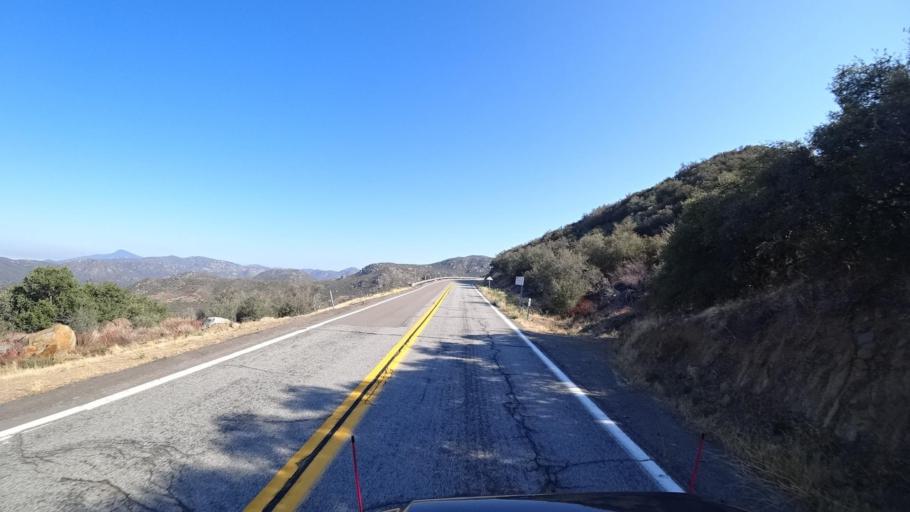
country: US
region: California
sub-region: San Diego County
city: Pine Valley
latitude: 32.8206
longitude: -116.5088
